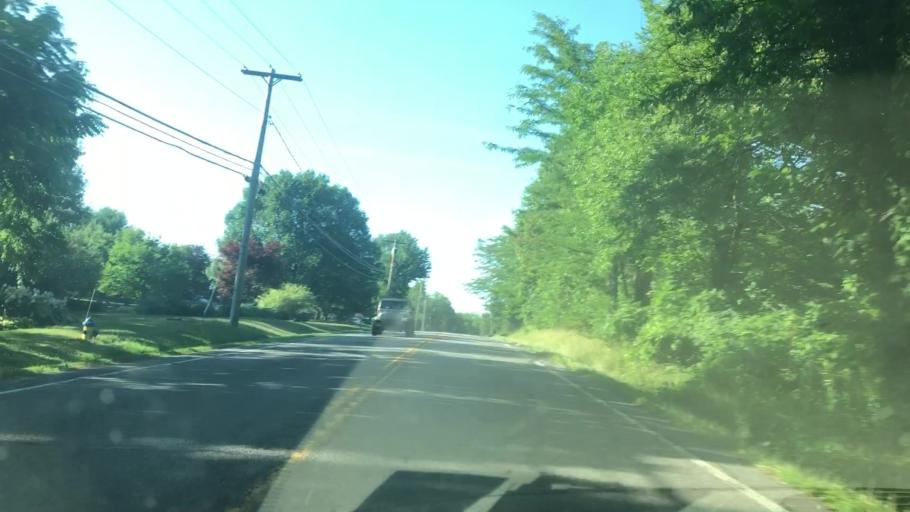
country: US
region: New York
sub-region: Wayne County
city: Ontario
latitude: 43.1505
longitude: -77.2927
